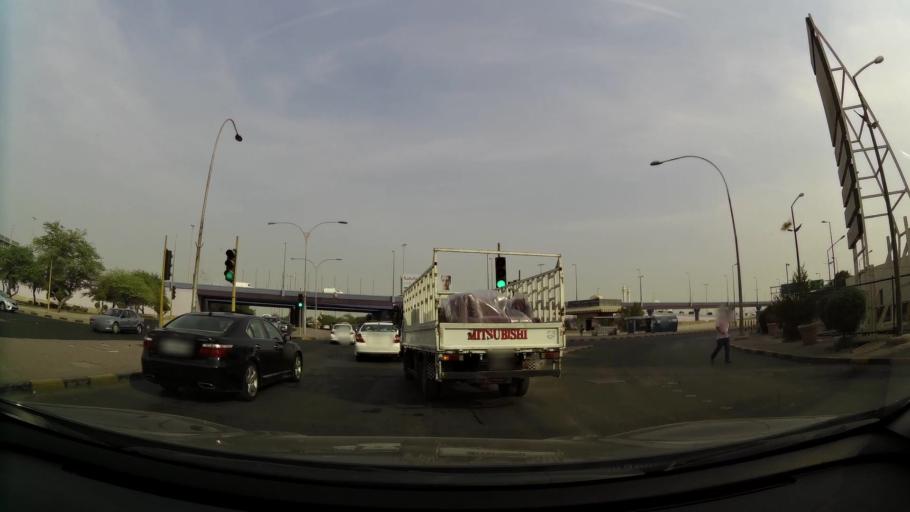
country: KW
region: Al Farwaniyah
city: Janub as Surrah
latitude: 29.2719
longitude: 47.9682
